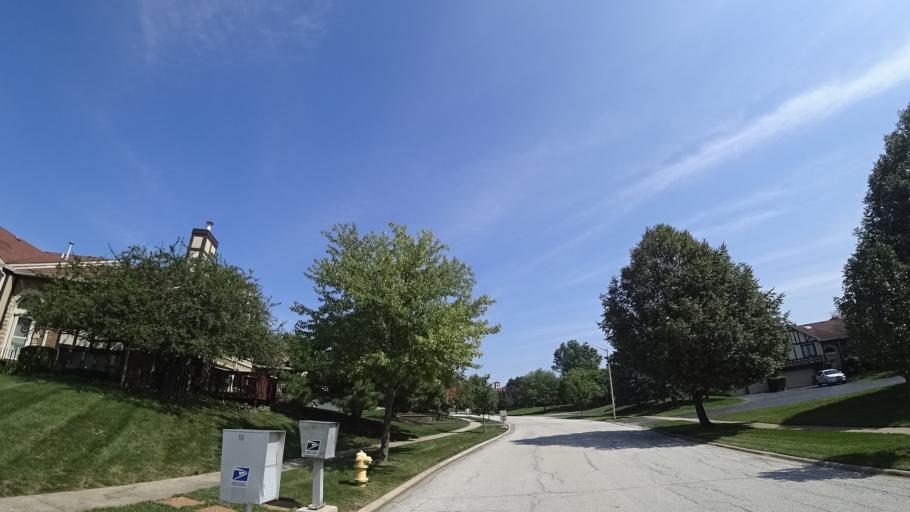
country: US
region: Illinois
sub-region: Cook County
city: Orland Hills
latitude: 41.5715
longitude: -87.8443
